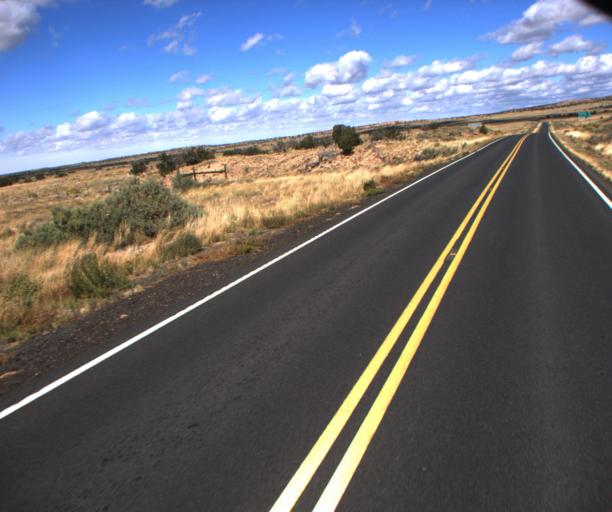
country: US
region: Arizona
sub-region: Apache County
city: Houck
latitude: 35.0487
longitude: -109.2734
